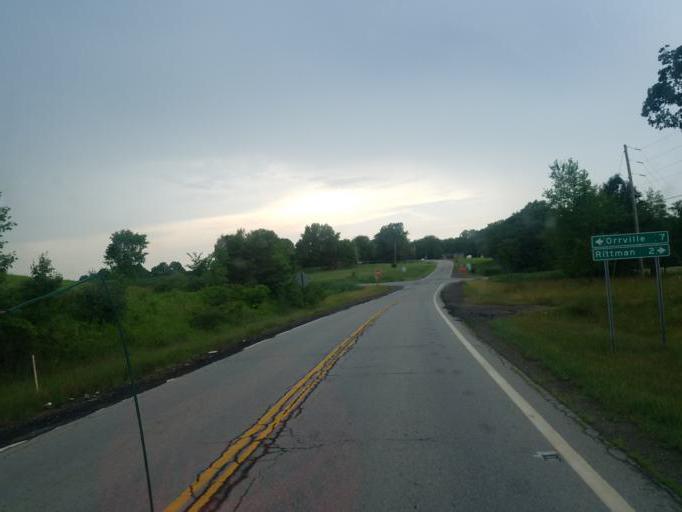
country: US
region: Ohio
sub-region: Wayne County
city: Rittman
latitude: 40.9459
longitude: -81.7621
